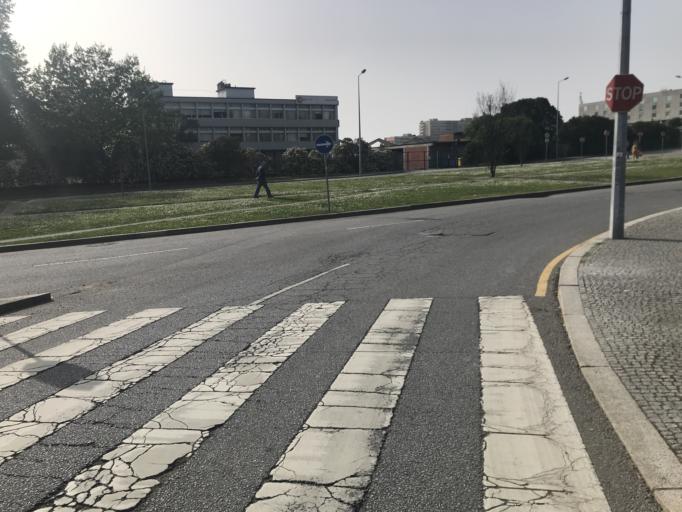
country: PT
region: Porto
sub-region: Matosinhos
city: Matosinhos
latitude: 41.1755
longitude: -8.6757
